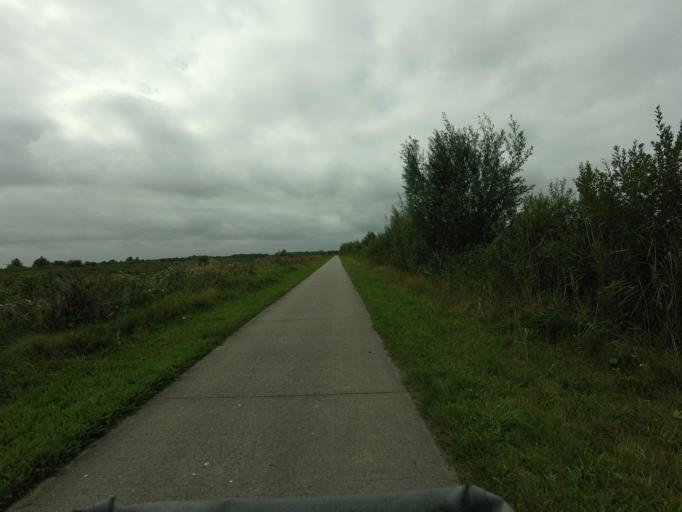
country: NL
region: Overijssel
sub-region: Gemeente Steenwijkerland
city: Giethoorn
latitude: 52.7136
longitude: 6.0655
